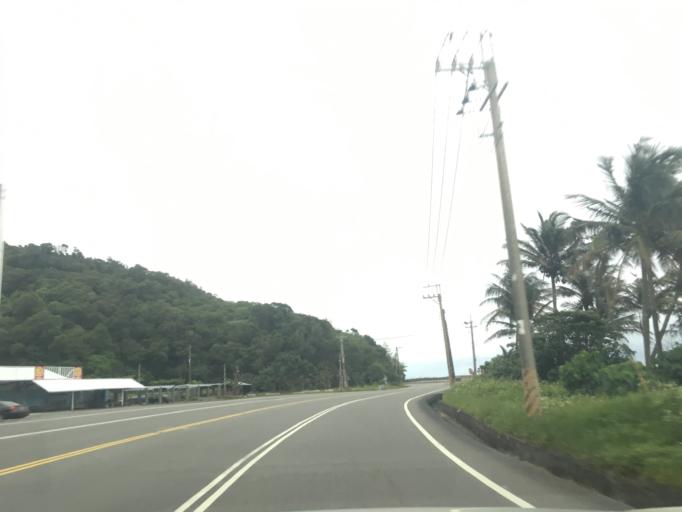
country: TW
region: Taiwan
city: Hengchun
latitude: 22.3307
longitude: 120.8924
